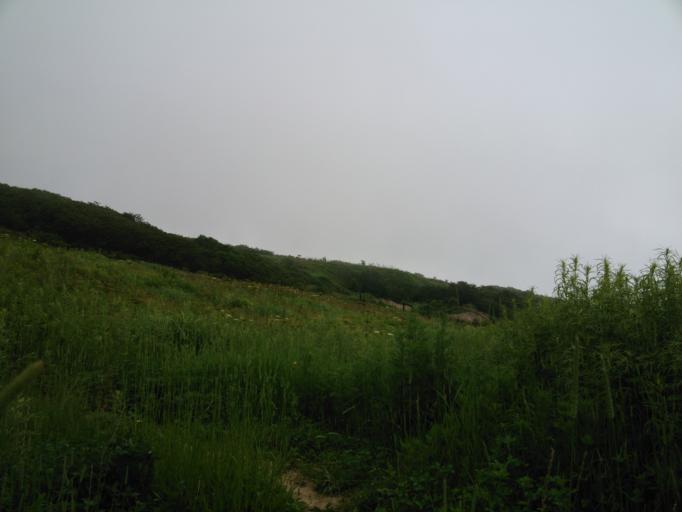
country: RU
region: Primorskiy
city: Vladivostok
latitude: 43.0944
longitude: 131.9882
